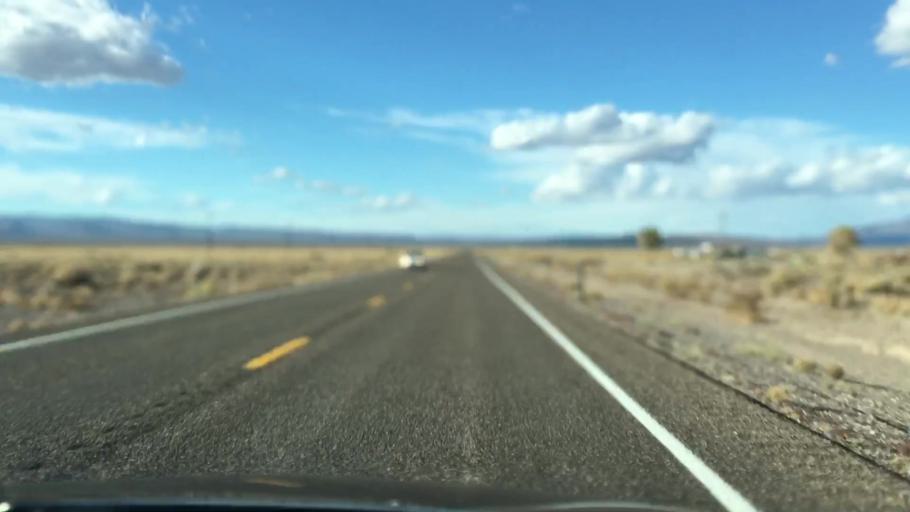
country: US
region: Nevada
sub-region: Nye County
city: Beatty
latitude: 37.2487
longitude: -117.0025
